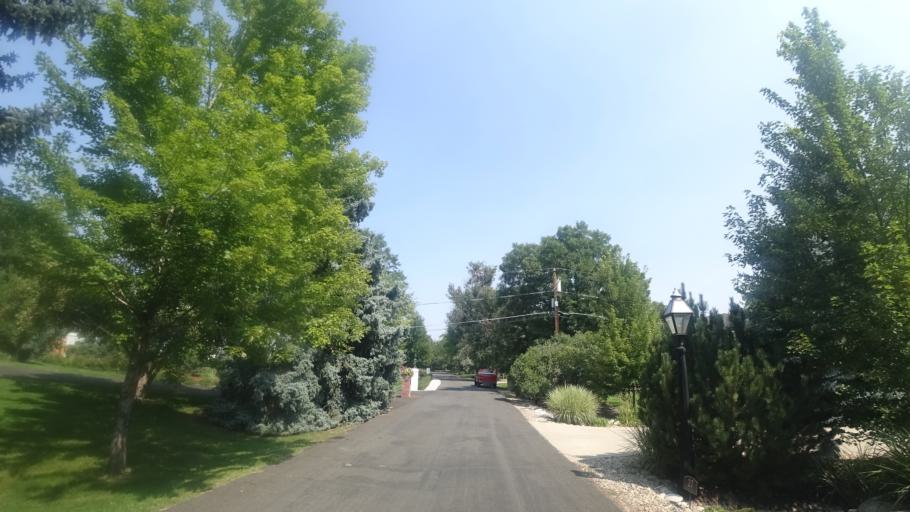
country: US
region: Colorado
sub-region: Arapahoe County
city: Cherry Hills Village
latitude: 39.6271
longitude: -104.9737
